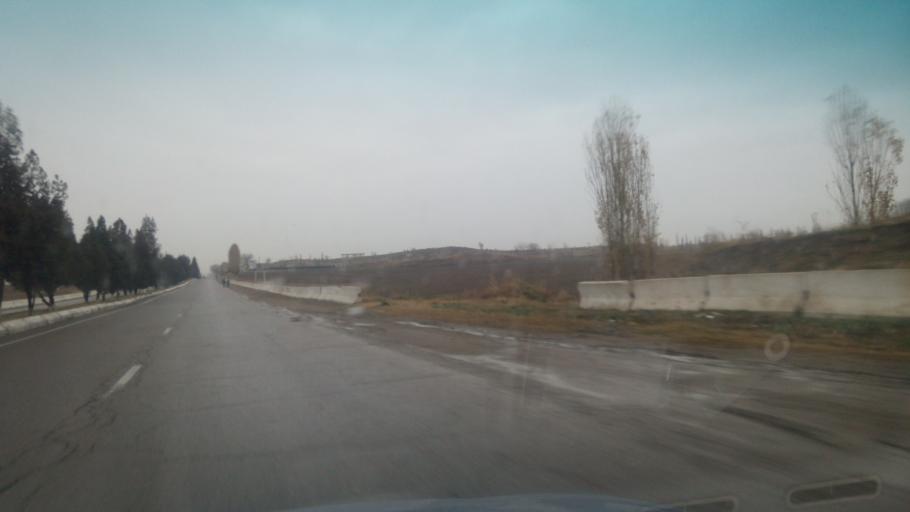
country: UZ
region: Toshkent
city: Zafar
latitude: 41.0421
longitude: 68.8835
